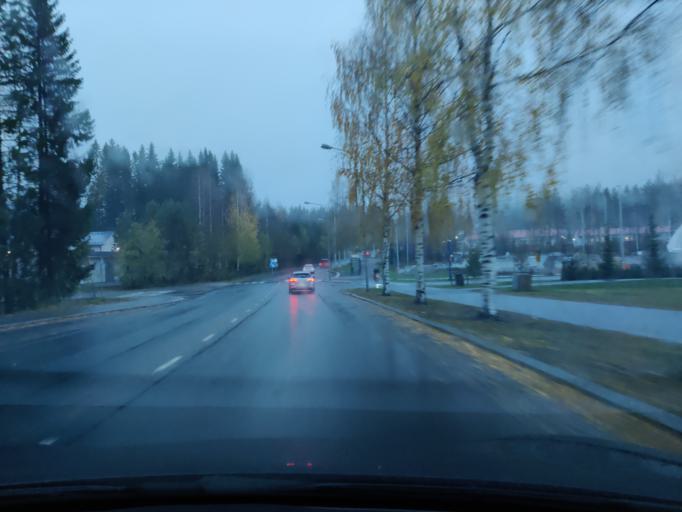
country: FI
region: Northern Savo
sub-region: Kuopio
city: Kuopio
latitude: 62.8396
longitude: 27.6566
